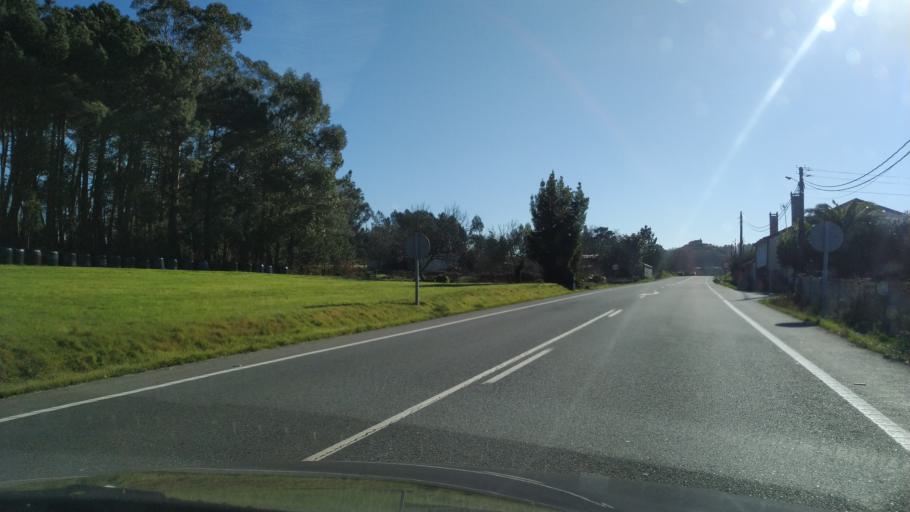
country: ES
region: Galicia
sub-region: Provincia da Coruna
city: Ribeira
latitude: 42.7516
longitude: -8.3515
